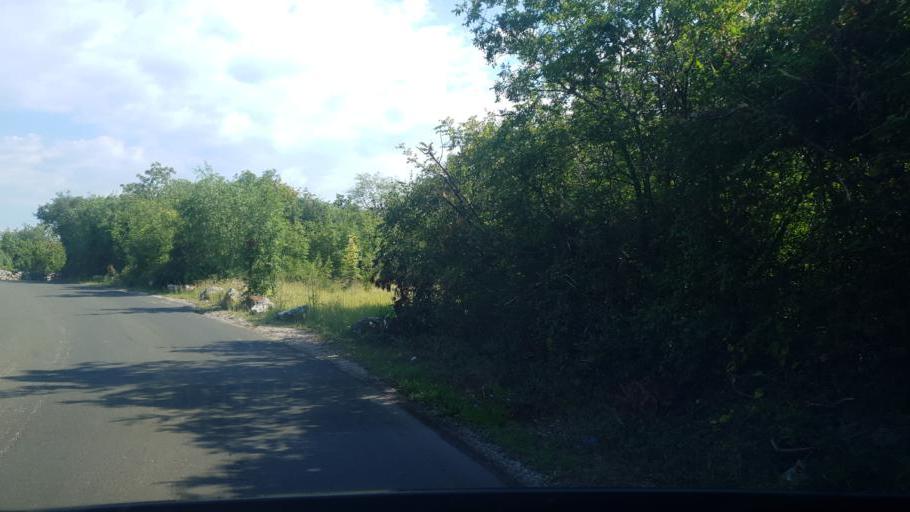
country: HR
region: Primorsko-Goranska
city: Omisalj
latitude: 45.1677
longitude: 14.5974
